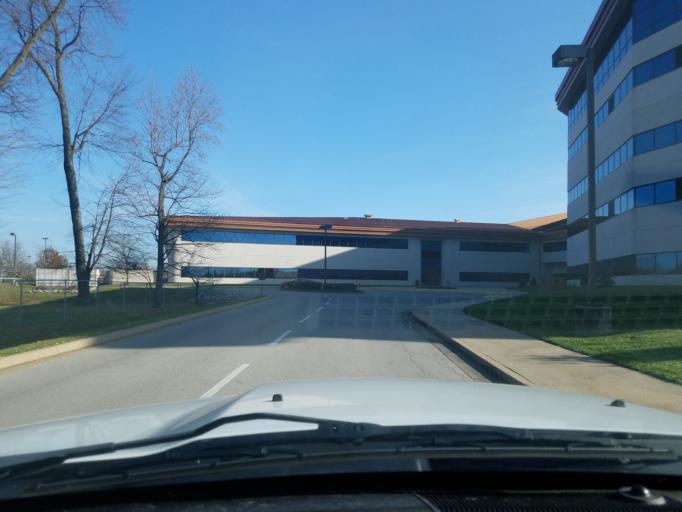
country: US
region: Kentucky
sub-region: Jefferson County
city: Douglass Hills
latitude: 38.2287
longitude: -85.5470
